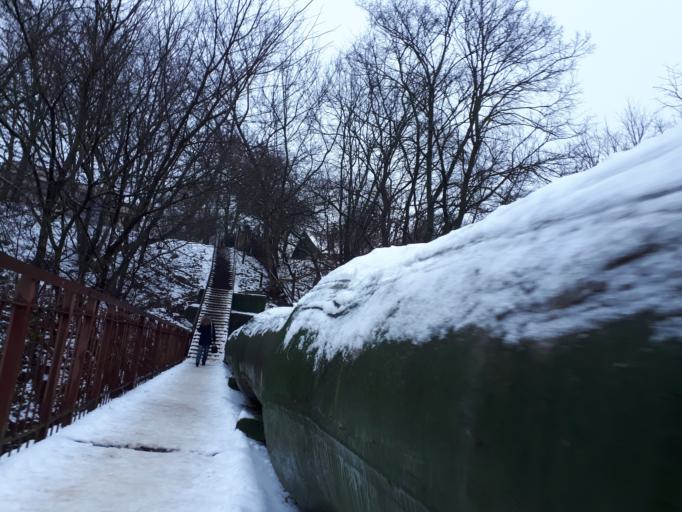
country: BY
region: Vitebsk
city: Vitebsk
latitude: 55.1908
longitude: 30.2199
